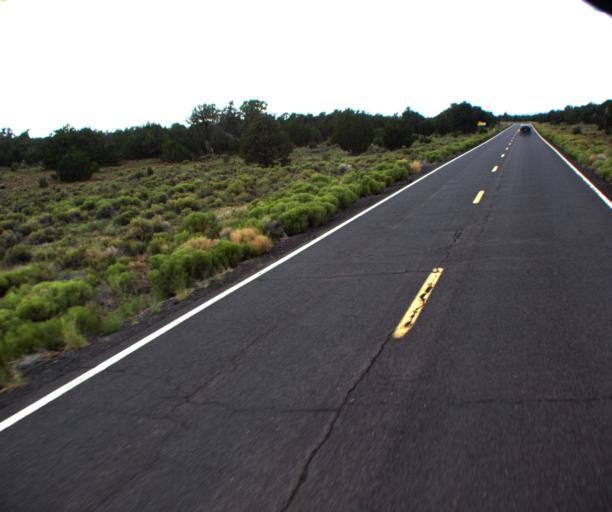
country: US
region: Arizona
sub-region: Coconino County
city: Parks
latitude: 35.5383
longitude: -111.8528
